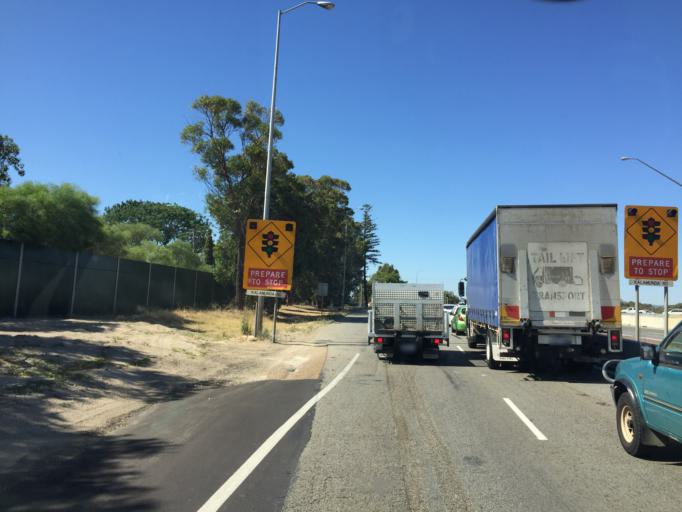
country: AU
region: Western Australia
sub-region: Kalamunda
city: Maida Vale
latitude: -31.9420
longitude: 116.0155
